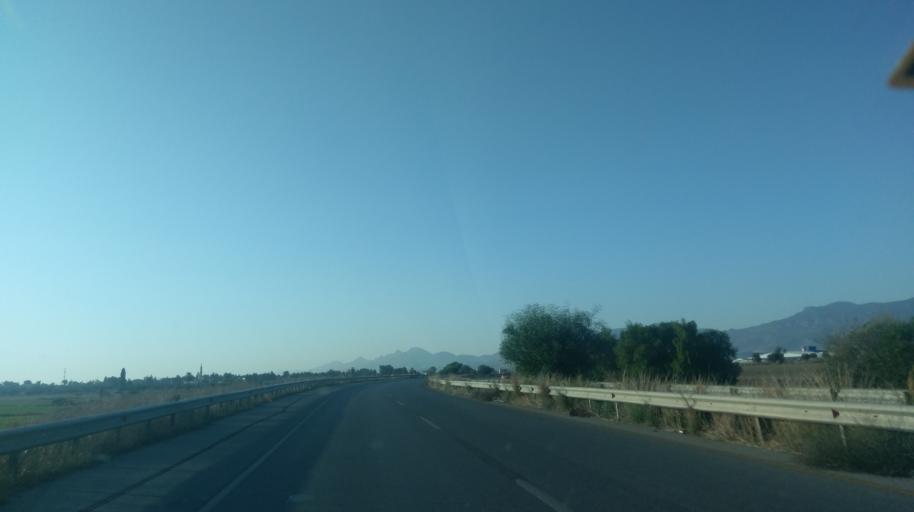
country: CY
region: Ammochostos
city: Lefkonoiko
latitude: 35.2023
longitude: 33.6014
